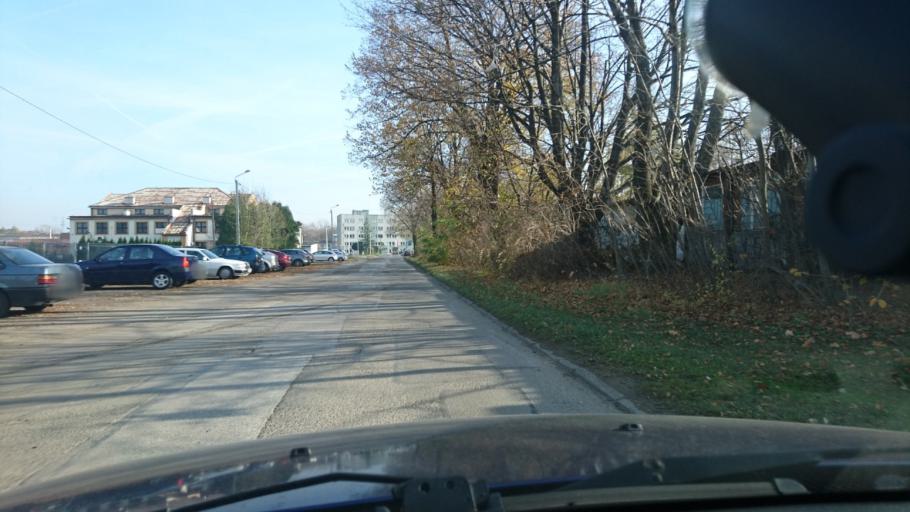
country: PL
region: Silesian Voivodeship
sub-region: Powiat bielski
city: Jaworze
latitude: 49.8113
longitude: 18.9814
